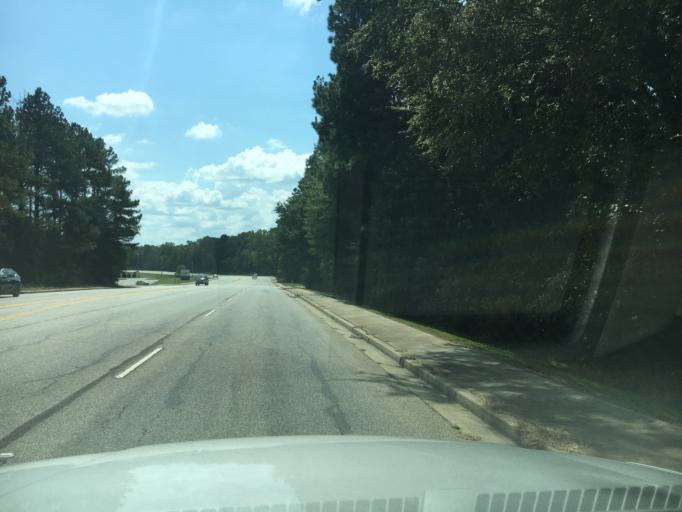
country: US
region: South Carolina
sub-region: Greenwood County
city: Greenwood
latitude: 34.2150
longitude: -82.2047
